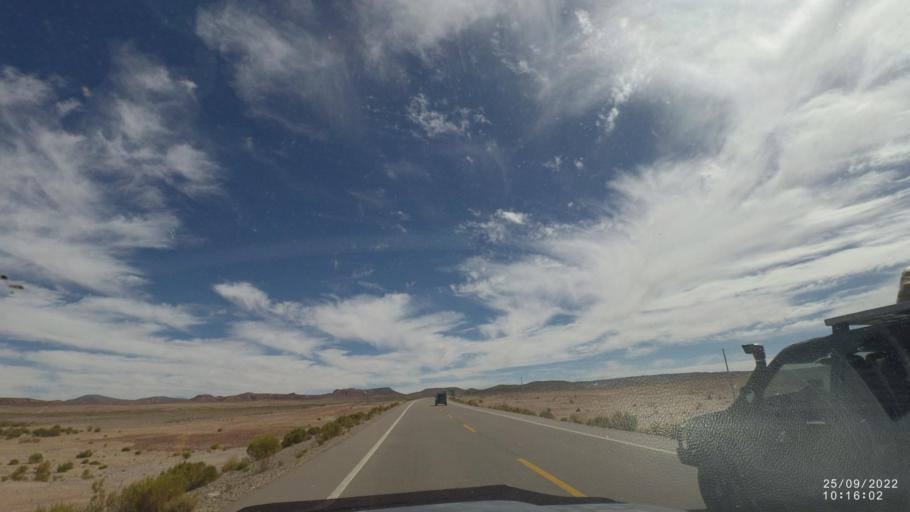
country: BO
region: Potosi
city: Colchani
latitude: -20.0375
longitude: -66.8701
